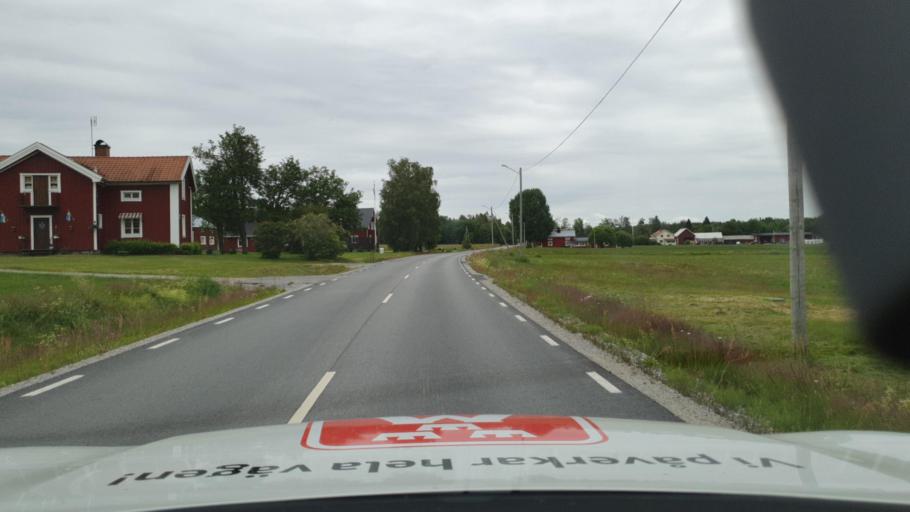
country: SE
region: Vaesterbotten
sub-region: Nordmalings Kommun
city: Nordmaling
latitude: 63.5348
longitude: 19.3659
